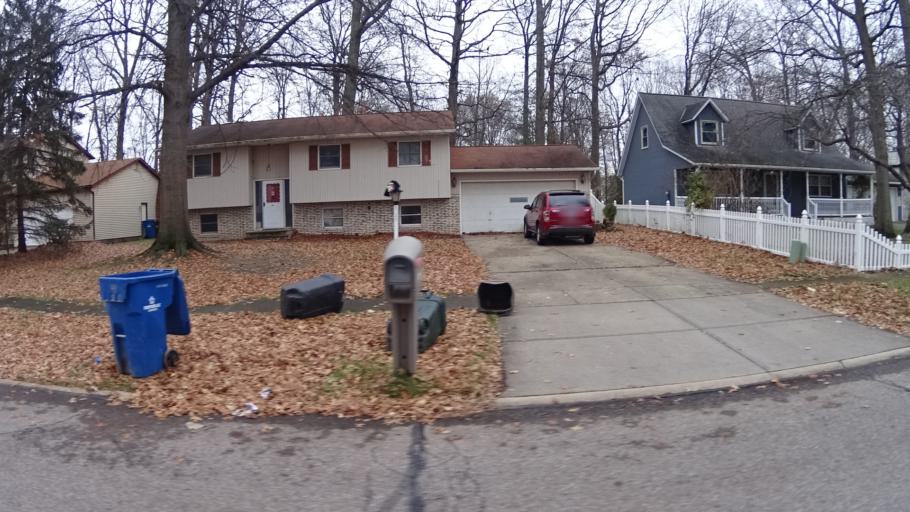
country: US
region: Ohio
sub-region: Lorain County
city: North Ridgeville
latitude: 41.3638
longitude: -81.9959
